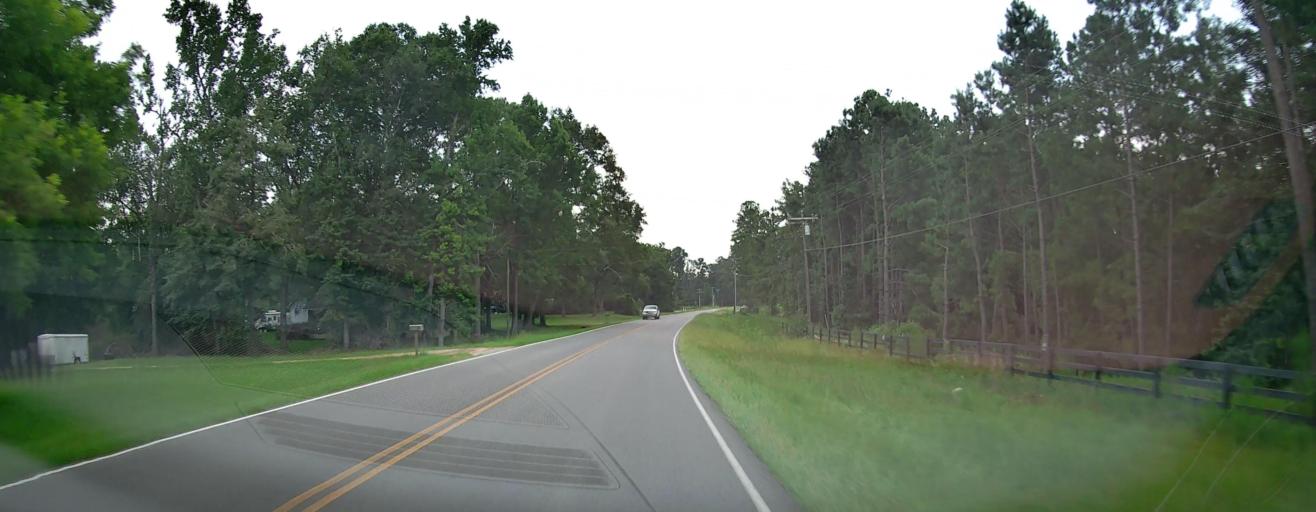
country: US
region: Georgia
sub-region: Laurens County
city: Dublin
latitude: 32.5734
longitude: -82.9083
